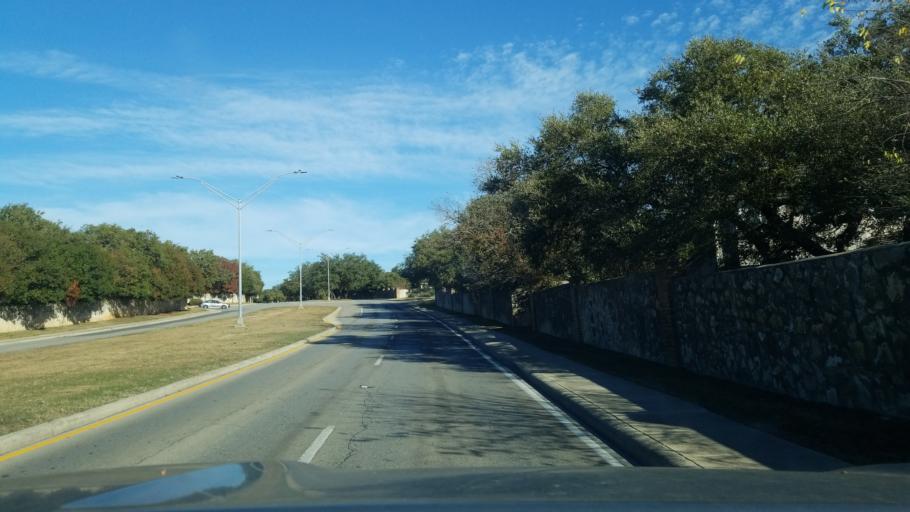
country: US
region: Texas
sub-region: Bexar County
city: Hollywood Park
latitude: 29.6032
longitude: -98.5219
